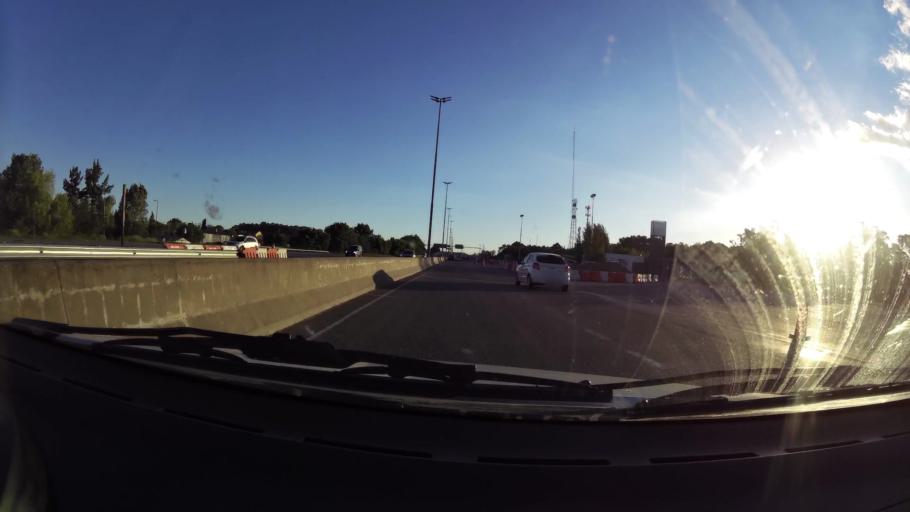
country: AR
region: Buenos Aires
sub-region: Partido de Quilmes
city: Quilmes
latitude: -34.7854
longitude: -58.1539
